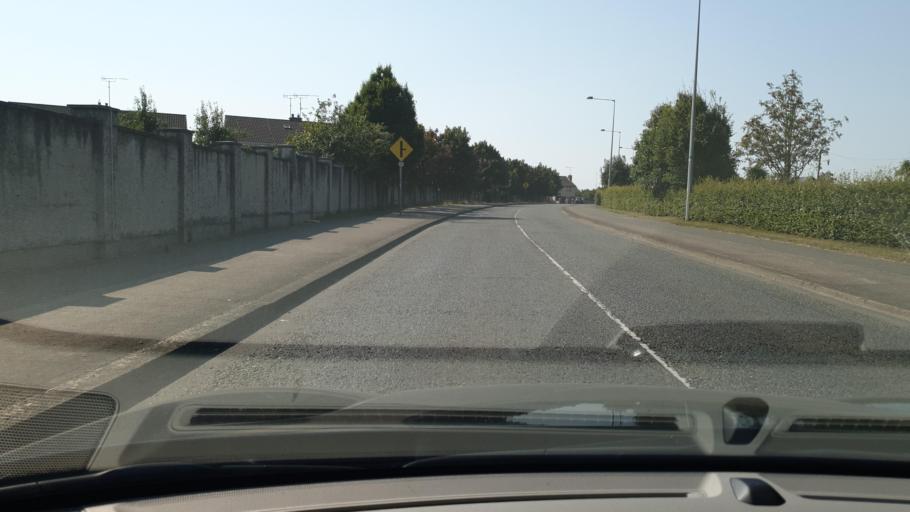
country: IE
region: Leinster
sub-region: An Mhi
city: Trim
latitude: 53.5624
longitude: -6.7951
